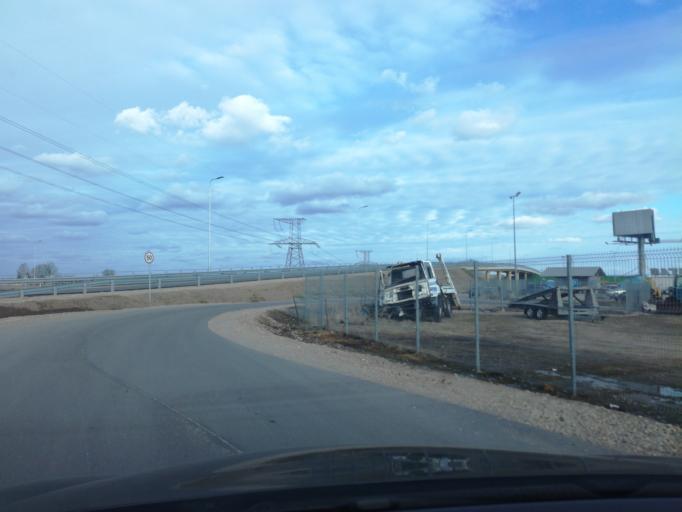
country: LT
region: Marijampoles apskritis
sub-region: Marijampole Municipality
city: Marijampole
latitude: 54.5956
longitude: 23.3904
